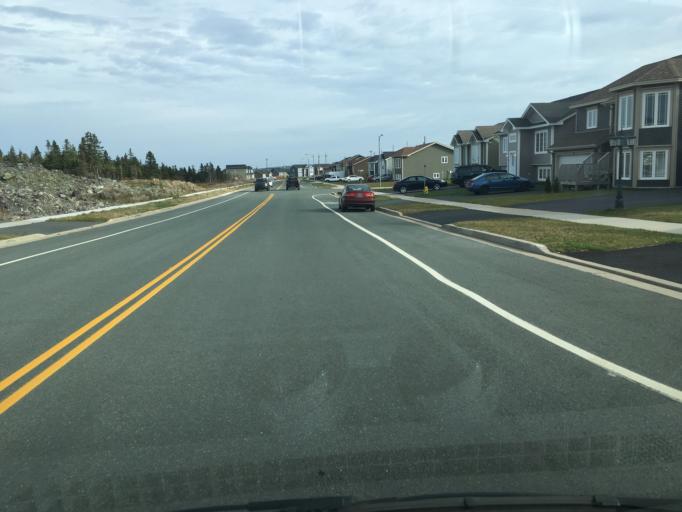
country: CA
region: Newfoundland and Labrador
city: Mount Pearl
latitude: 47.5550
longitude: -52.7970
